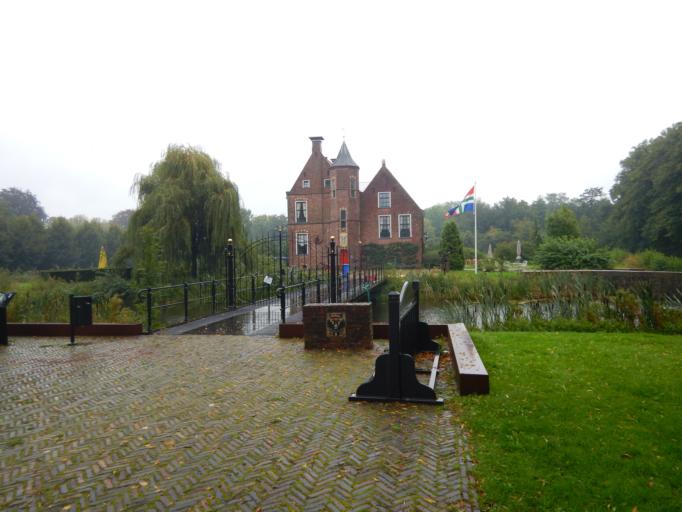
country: NL
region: Groningen
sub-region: Gemeente Vlagtwedde
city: Vlagtwedde
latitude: 53.0670
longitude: 7.0721
